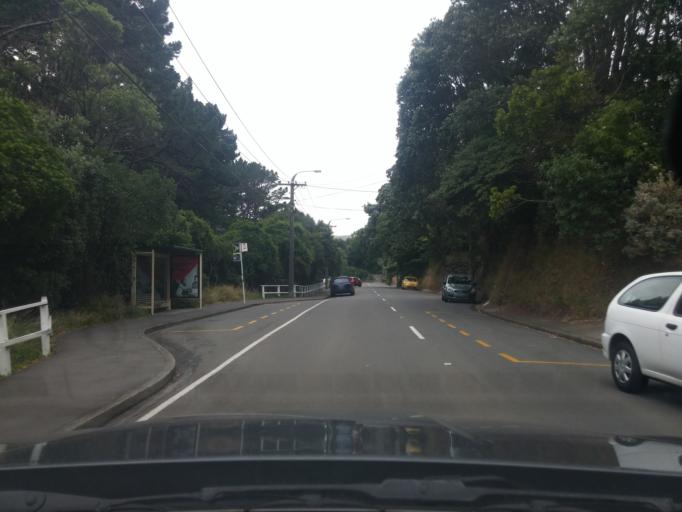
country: NZ
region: Wellington
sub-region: Wellington City
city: Kelburn
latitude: -41.2647
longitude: 174.7641
